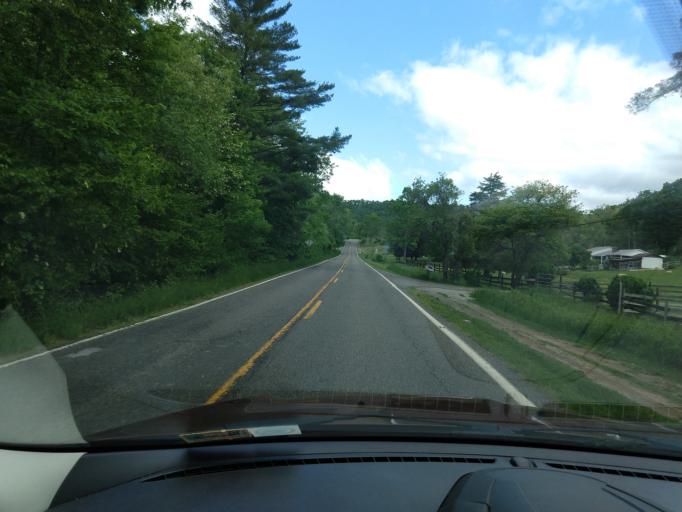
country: US
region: Virginia
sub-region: City of Galax
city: Galax
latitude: 36.7916
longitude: -80.9863
